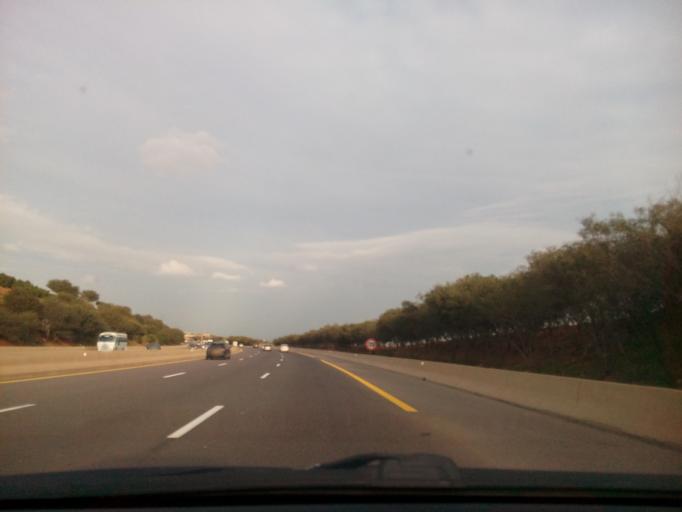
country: DZ
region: Relizane
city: Relizane
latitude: 35.7422
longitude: 0.3406
